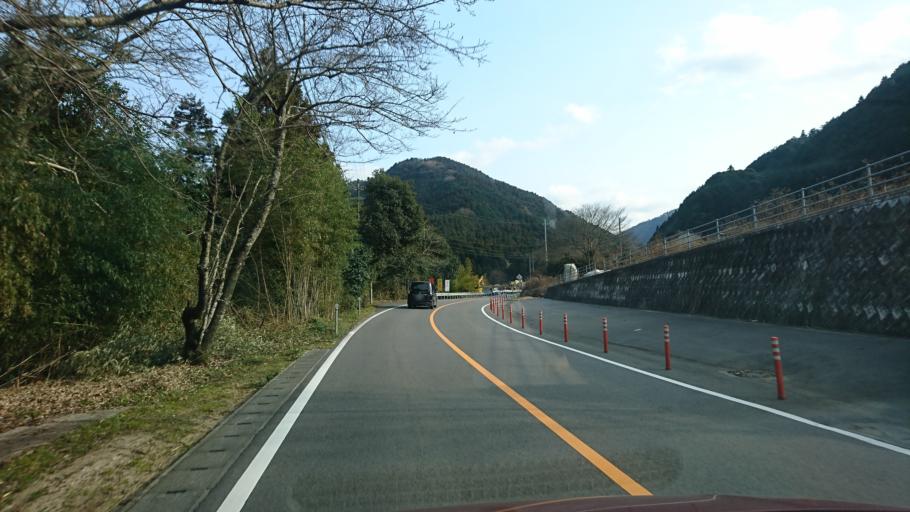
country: JP
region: Ehime
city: Hojo
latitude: 33.9692
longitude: 132.9035
